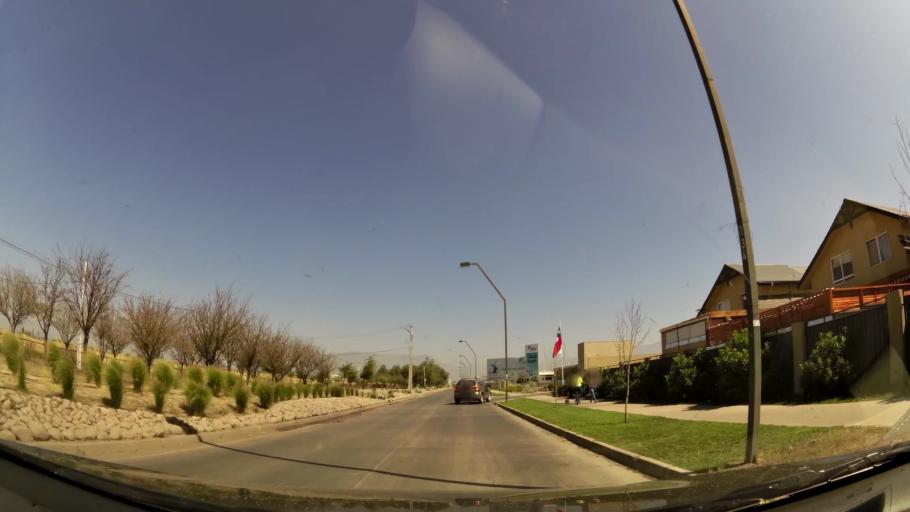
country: CL
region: Santiago Metropolitan
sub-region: Provincia de Chacabuco
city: Chicureo Abajo
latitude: -33.3277
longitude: -70.7579
